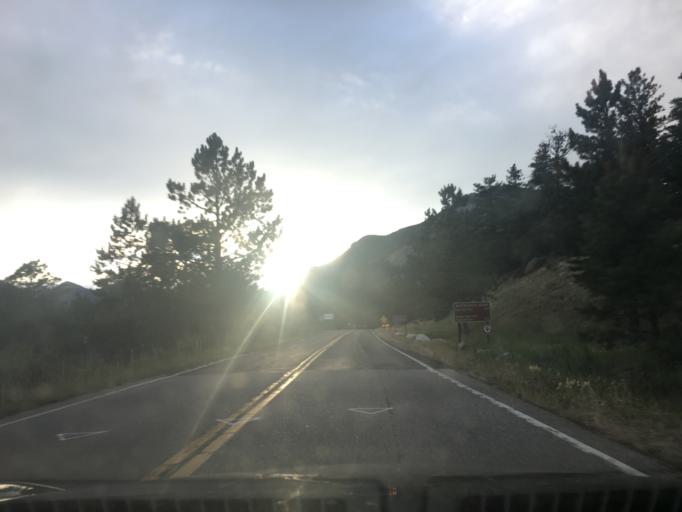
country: US
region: Colorado
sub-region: Larimer County
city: Estes Park
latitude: 40.4031
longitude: -105.5887
